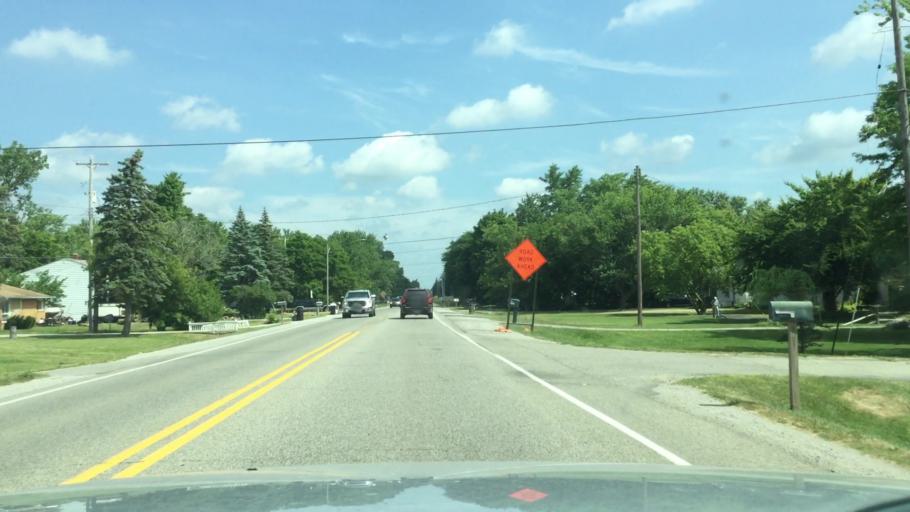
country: US
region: Michigan
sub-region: Genesee County
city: Flushing
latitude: 43.0626
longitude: -83.8132
